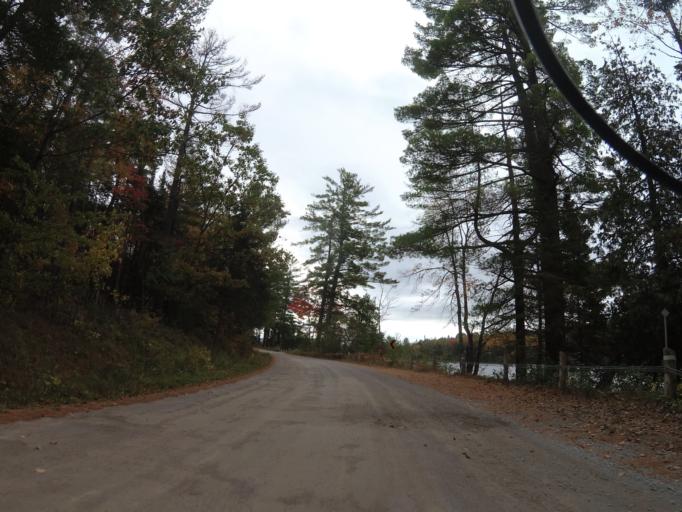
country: CA
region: Ontario
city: Renfrew
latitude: 45.2596
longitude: -77.1943
